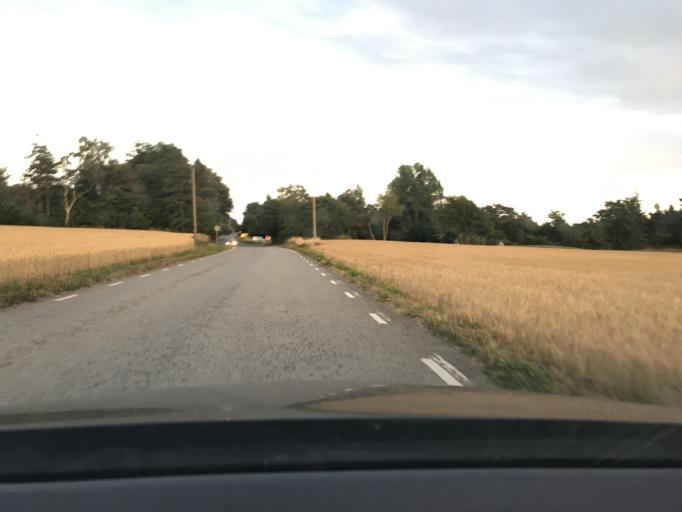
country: SE
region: Skane
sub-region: Simrishamns Kommun
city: Simrishamn
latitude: 55.4369
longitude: 14.2289
